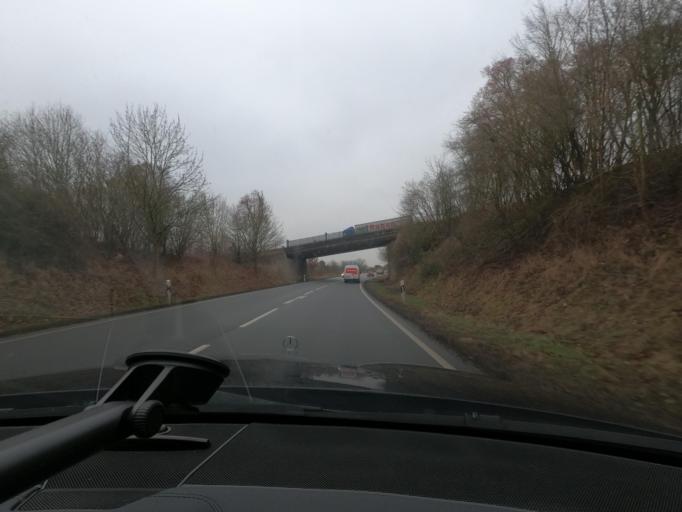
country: DE
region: Hesse
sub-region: Regierungsbezirk Kassel
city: Bad Arolsen
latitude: 51.3828
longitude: 8.9945
